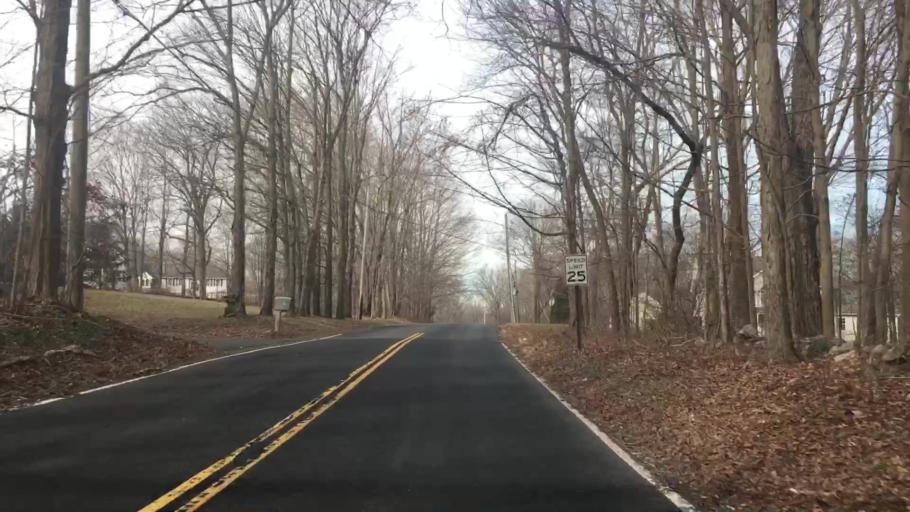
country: US
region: Connecticut
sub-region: Fairfield County
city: Newtown
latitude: 41.3649
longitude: -73.2414
